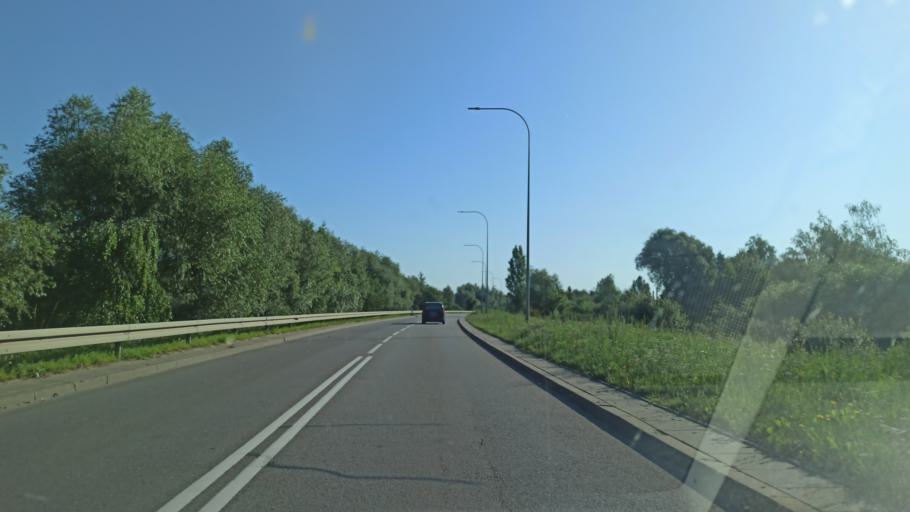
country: PL
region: Warmian-Masurian Voivodeship
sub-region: Powiat elblaski
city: Elblag
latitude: 54.1685
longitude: 19.3787
